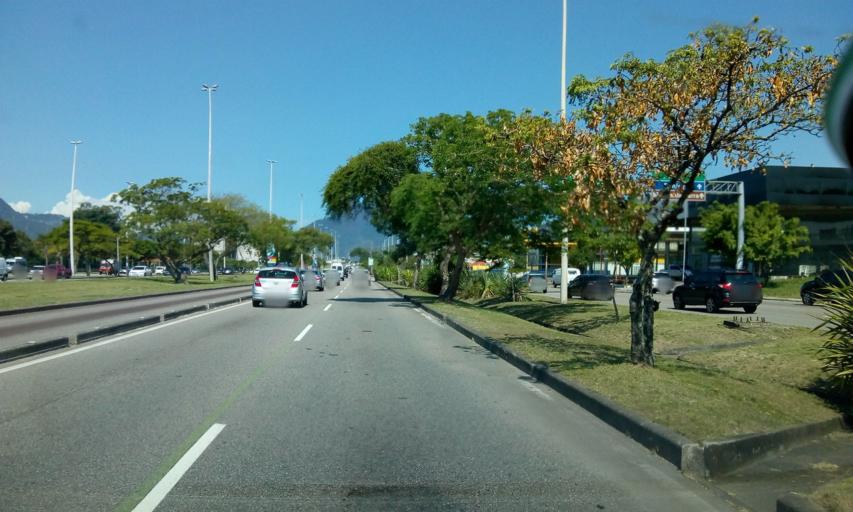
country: BR
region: Rio de Janeiro
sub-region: Rio De Janeiro
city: Rio de Janeiro
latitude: -23.0004
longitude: -43.3742
